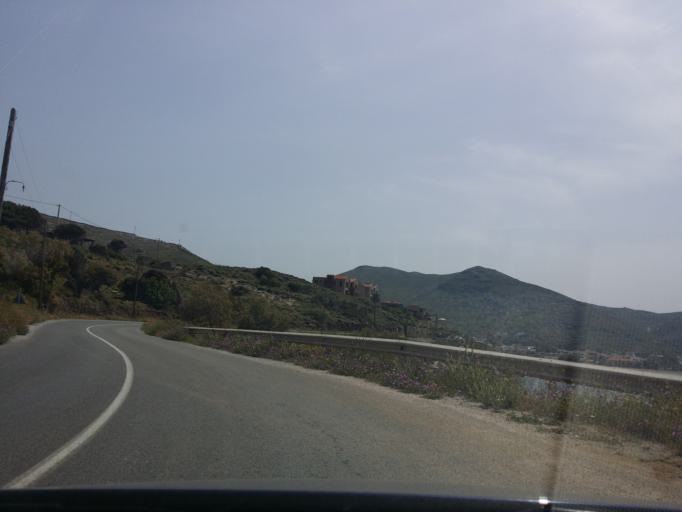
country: GR
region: South Aegean
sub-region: Nomos Kykladon
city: Kea
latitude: 37.6622
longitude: 24.3186
